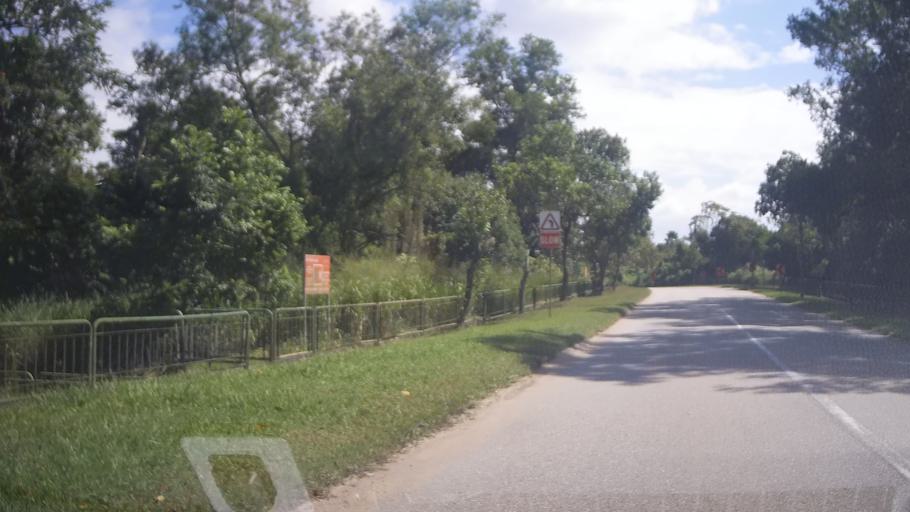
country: MY
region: Johor
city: Johor Bahru
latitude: 1.4284
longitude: 103.7087
